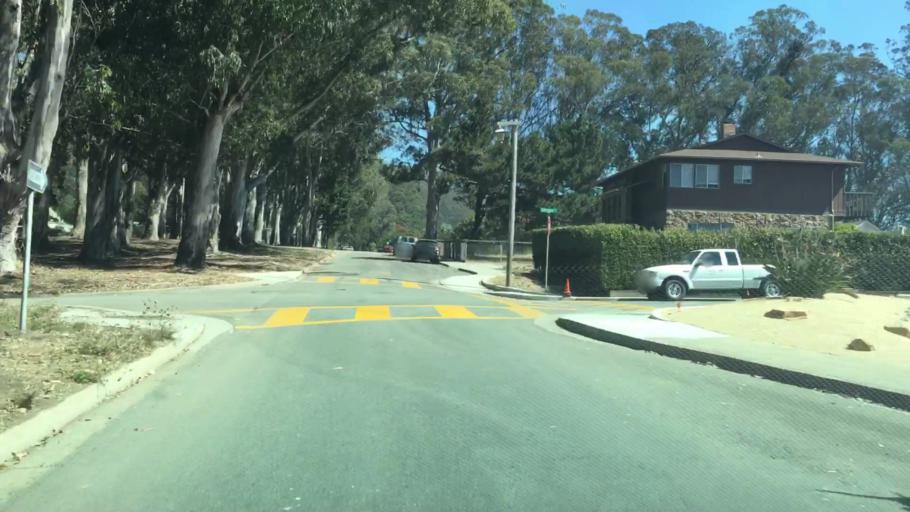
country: US
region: California
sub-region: San Mateo County
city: El Granada
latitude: 37.5013
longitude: -122.4672
